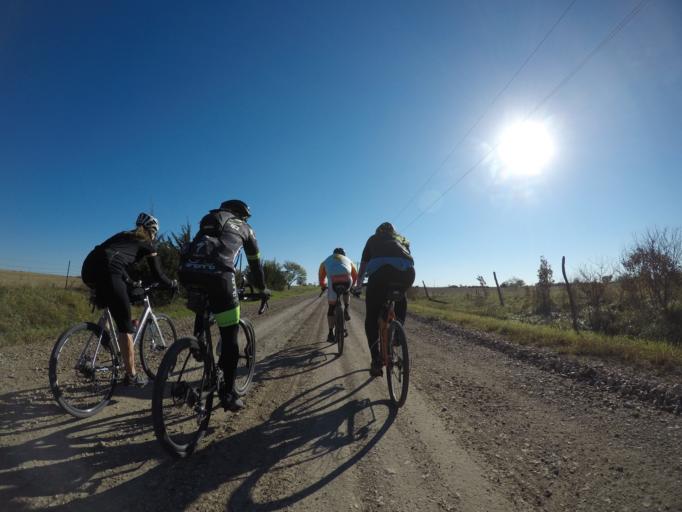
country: US
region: Kansas
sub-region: Morris County
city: Council Grove
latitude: 38.8260
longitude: -96.4719
